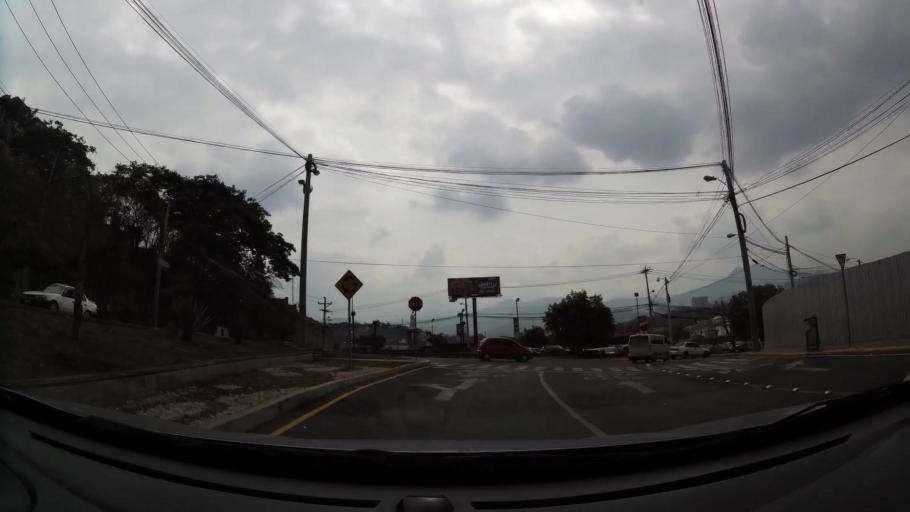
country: HN
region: Francisco Morazan
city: Tegucigalpa
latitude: 14.0895
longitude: -87.1744
